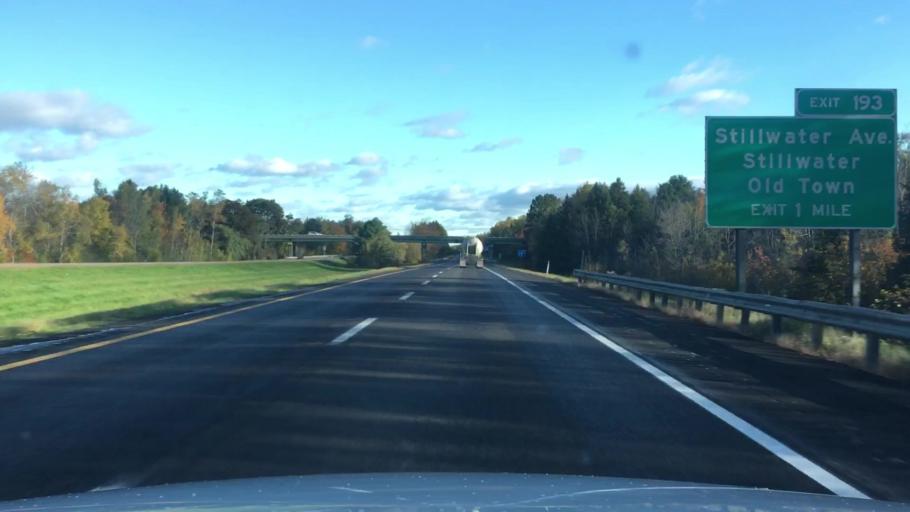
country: US
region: Maine
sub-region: Penobscot County
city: Orono
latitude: 44.8873
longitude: -68.6941
